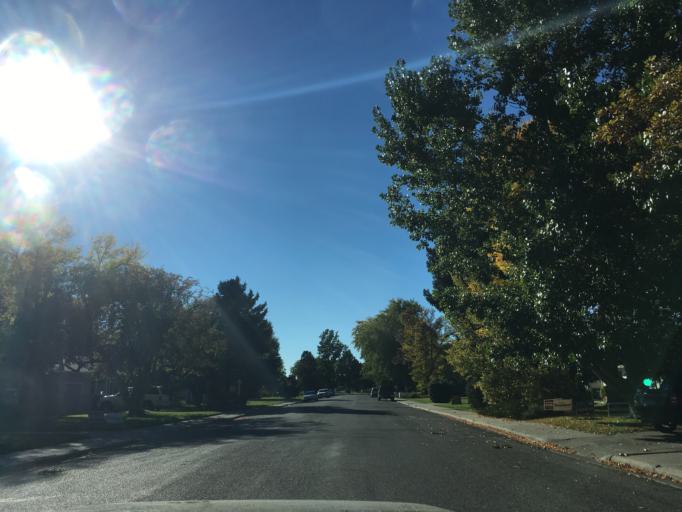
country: US
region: Montana
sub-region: Yellowstone County
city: Billings
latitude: 45.7908
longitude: -108.5382
